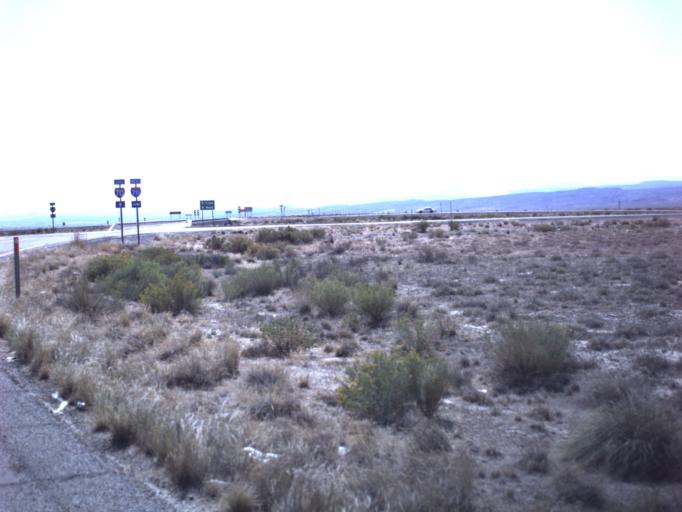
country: US
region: Utah
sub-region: Grand County
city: Moab
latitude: 38.9395
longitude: -109.4089
